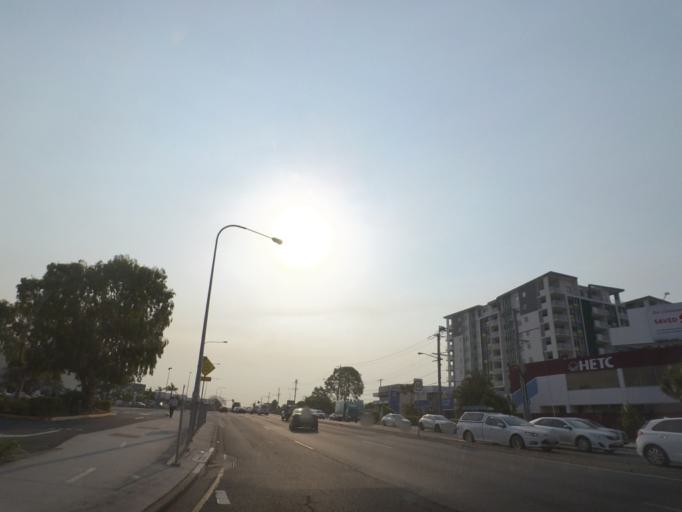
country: AU
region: Queensland
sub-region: Brisbane
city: Upper Mount Gravatt
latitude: -27.5601
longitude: 153.0811
